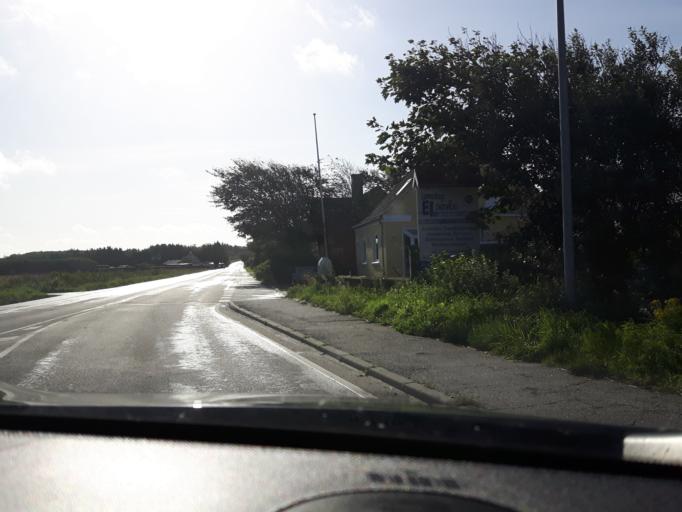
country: DK
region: North Denmark
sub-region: Hjorring Kommune
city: Hjorring
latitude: 57.4664
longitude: 9.8084
